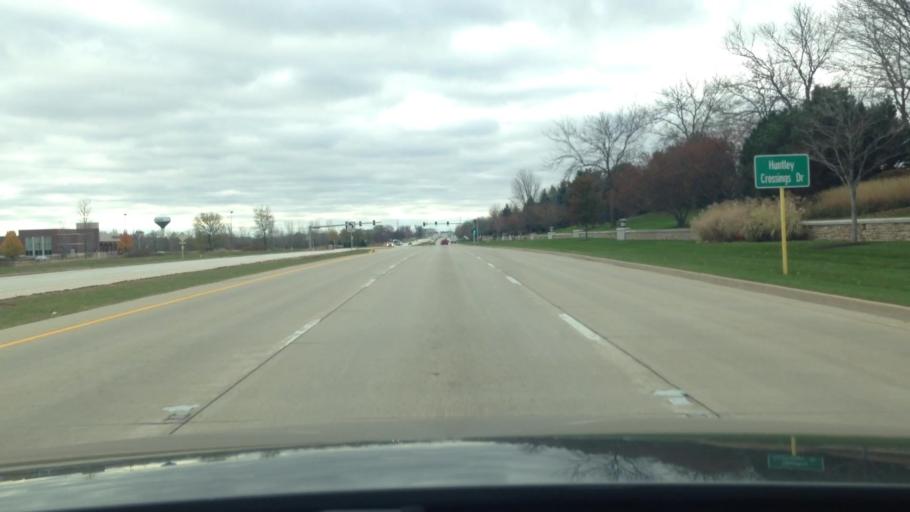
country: US
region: Illinois
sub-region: McHenry County
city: Huntley
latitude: 42.1442
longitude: -88.4329
